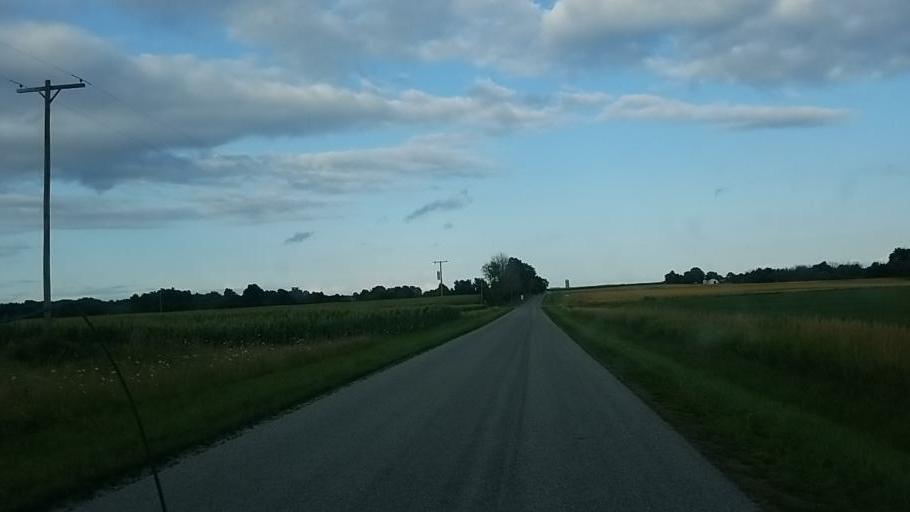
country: US
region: Michigan
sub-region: Montcalm County
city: Howard City
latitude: 43.3373
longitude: -85.3657
